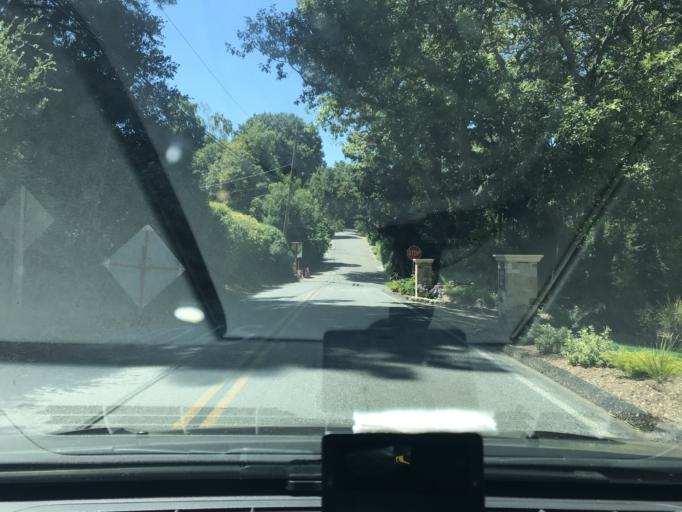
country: US
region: California
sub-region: Santa Clara County
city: Monte Sereno
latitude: 37.2298
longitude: -121.9950
